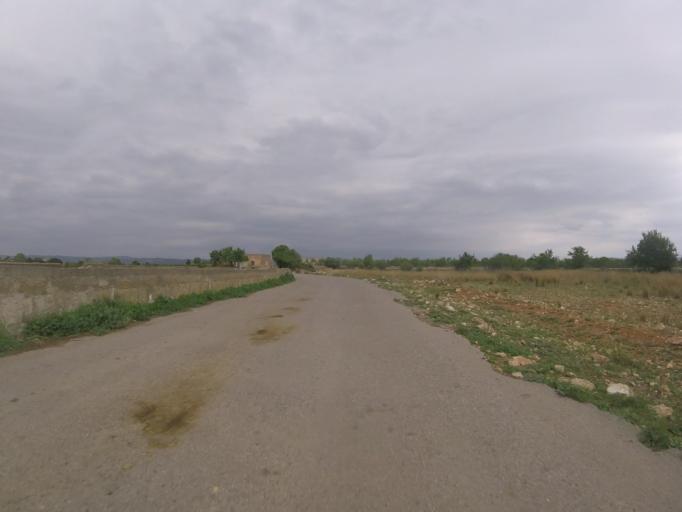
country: ES
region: Valencia
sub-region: Provincia de Castello
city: Torreblanca
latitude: 40.2139
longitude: 0.2399
